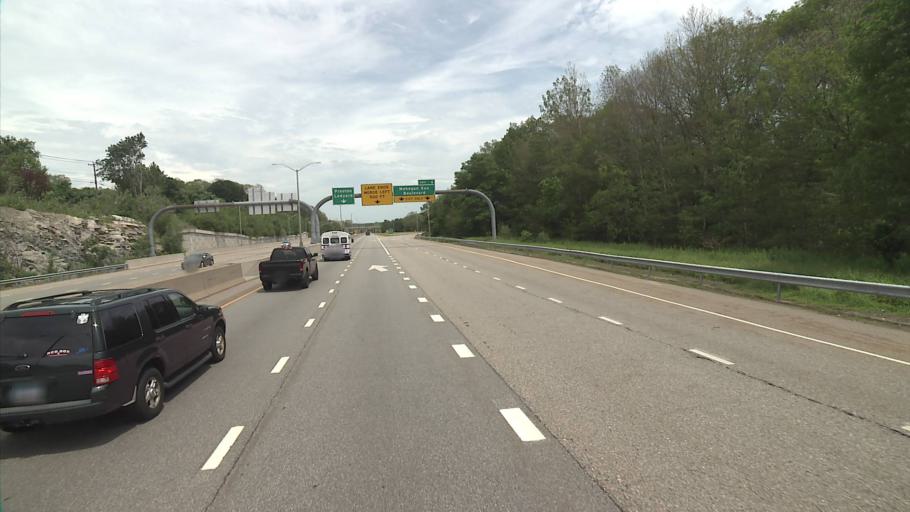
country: US
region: Connecticut
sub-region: New London County
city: Norwich
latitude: 41.4809
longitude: -72.0857
